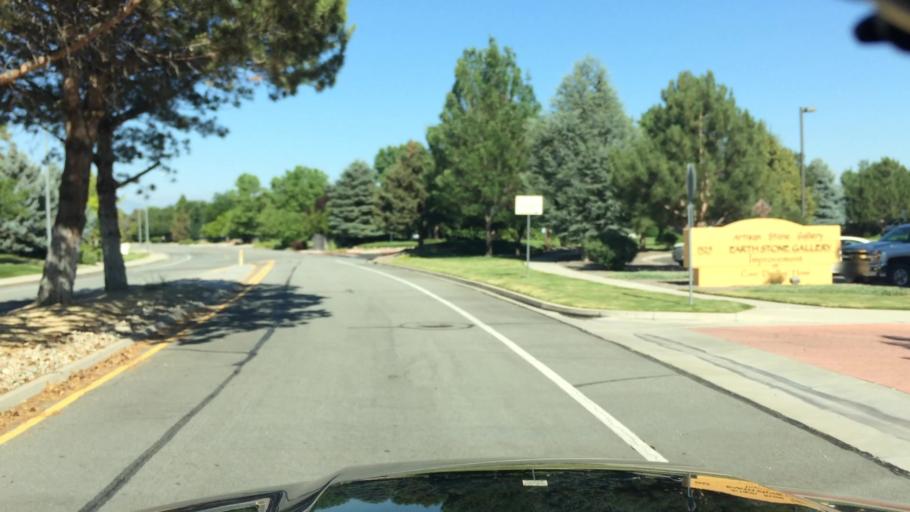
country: US
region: Nevada
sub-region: Washoe County
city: Sparks
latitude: 39.5059
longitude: -119.7486
